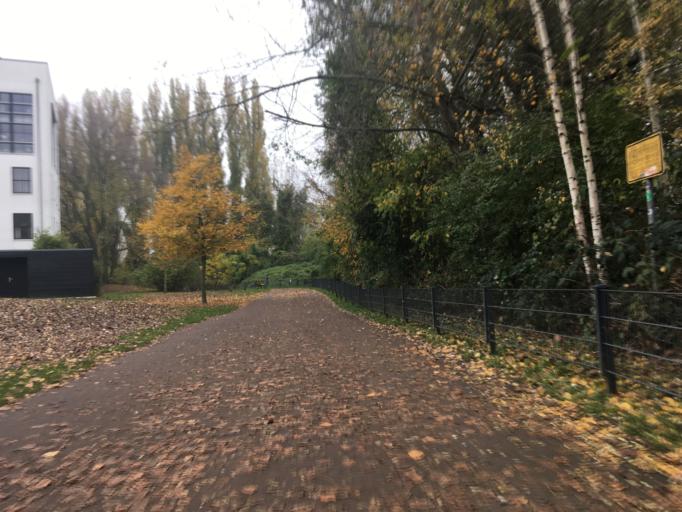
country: DE
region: Berlin
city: Rummelsburg
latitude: 52.4942
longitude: 13.4827
